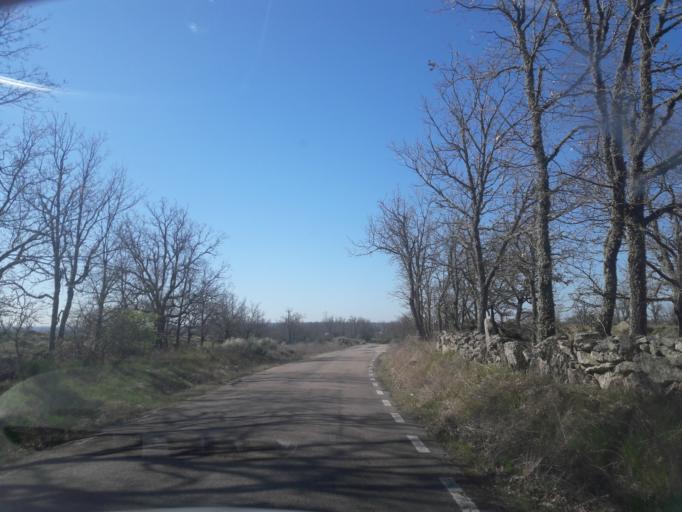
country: ES
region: Castille and Leon
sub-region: Provincia de Salamanca
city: Valsalabroso
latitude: 41.1137
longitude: -6.4833
